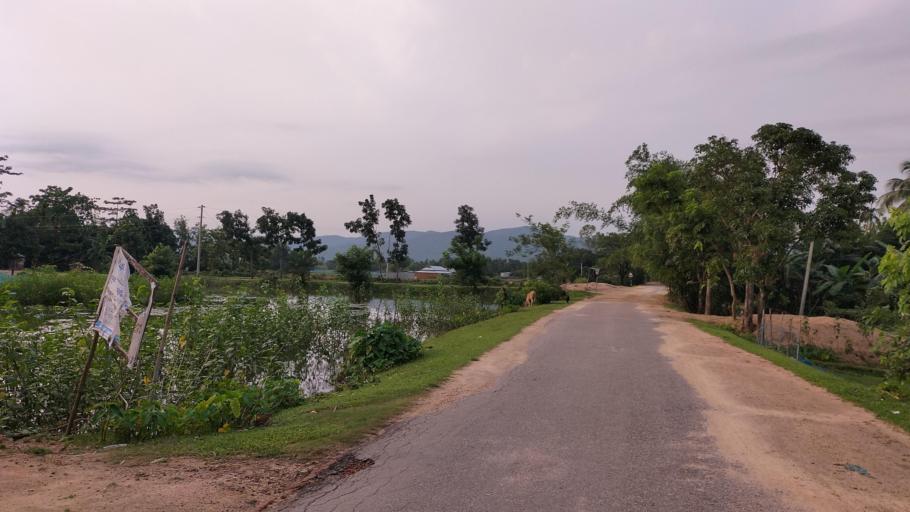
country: BD
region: Dhaka
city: Netrakona
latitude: 25.1318
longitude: 90.9131
